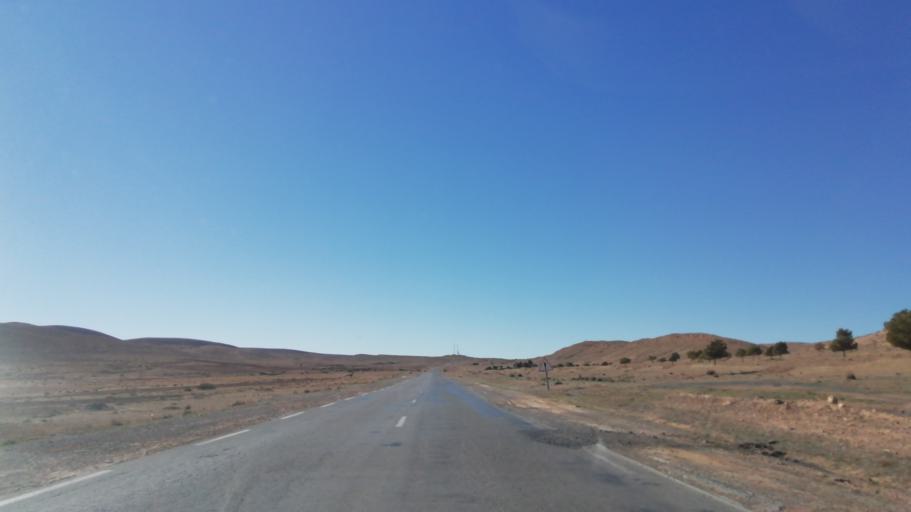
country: DZ
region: El Bayadh
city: El Bayadh
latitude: 33.6756
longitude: 1.4470
